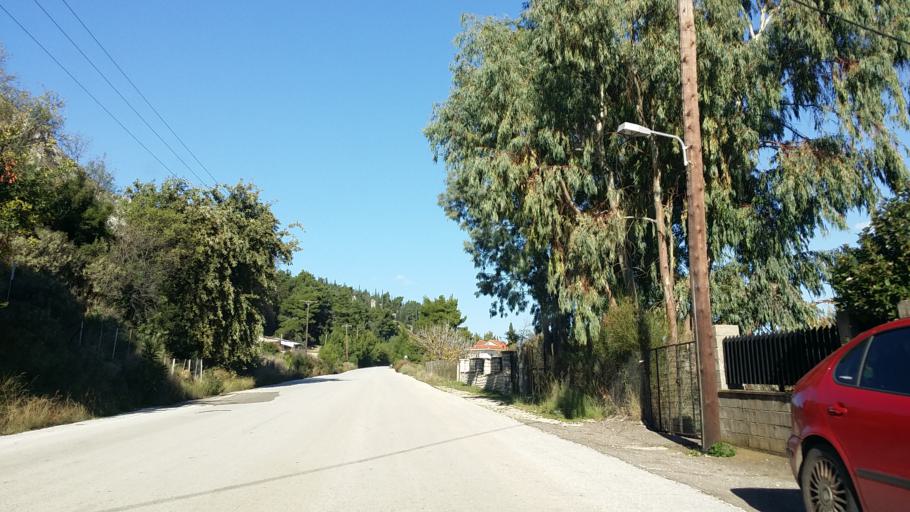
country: GR
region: West Greece
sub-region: Nomos Aitolias kai Akarnanias
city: Astakos
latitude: 38.5317
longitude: 21.0726
